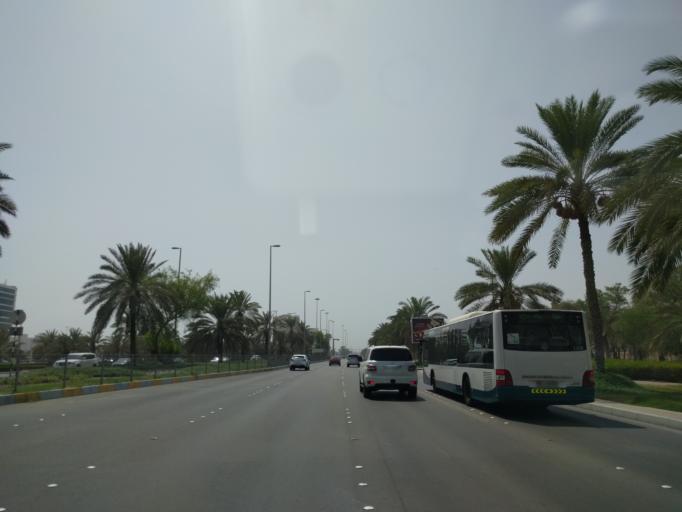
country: AE
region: Abu Dhabi
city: Abu Dhabi
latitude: 24.4361
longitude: 54.4207
